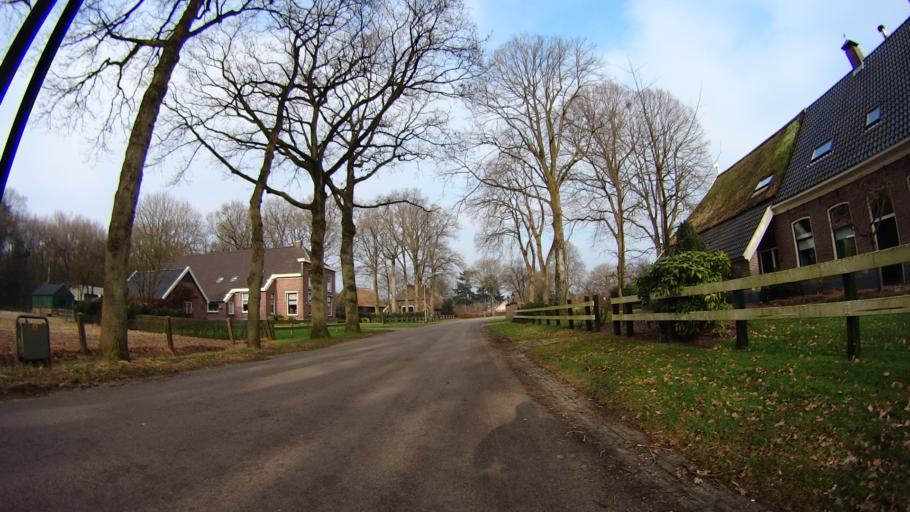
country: NL
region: Drenthe
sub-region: Gemeente Coevorden
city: Sleen
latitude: 52.7497
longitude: 6.8138
